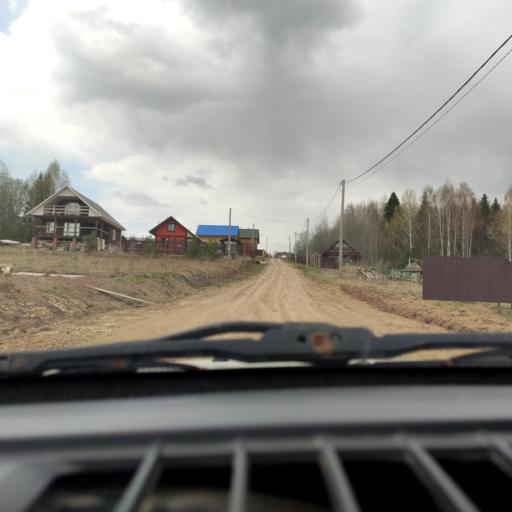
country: RU
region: Perm
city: Polazna
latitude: 58.3517
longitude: 56.2780
